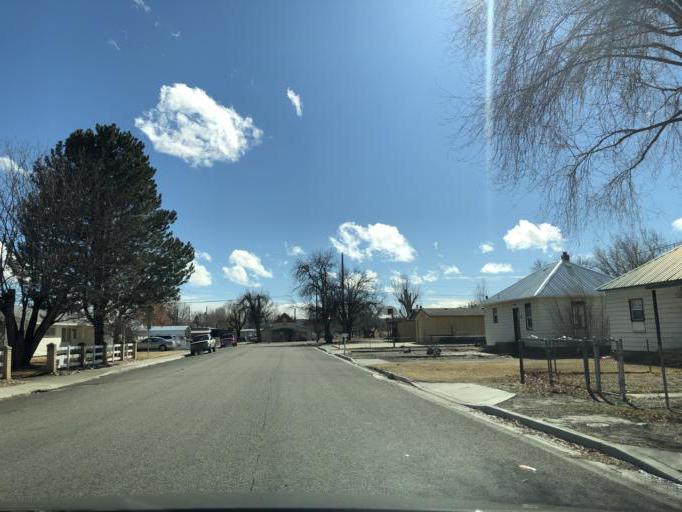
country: US
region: Utah
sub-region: Carbon County
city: East Carbon City
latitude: 38.9916
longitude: -110.1599
